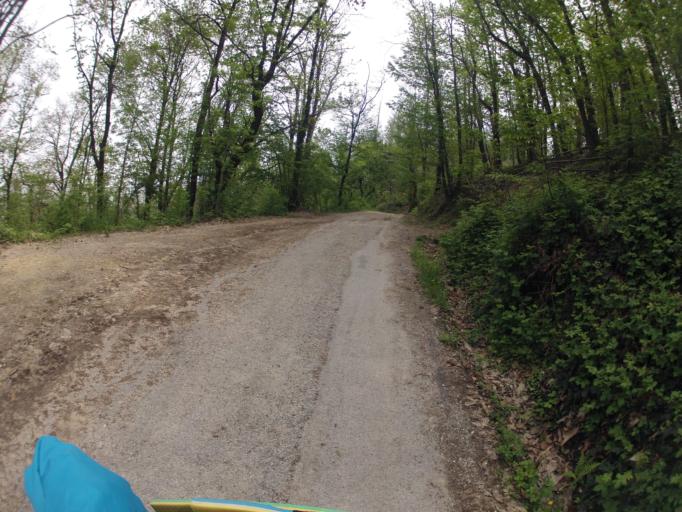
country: IT
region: Piedmont
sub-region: Provincia di Cuneo
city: Peveragno
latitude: 44.3322
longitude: 7.6120
